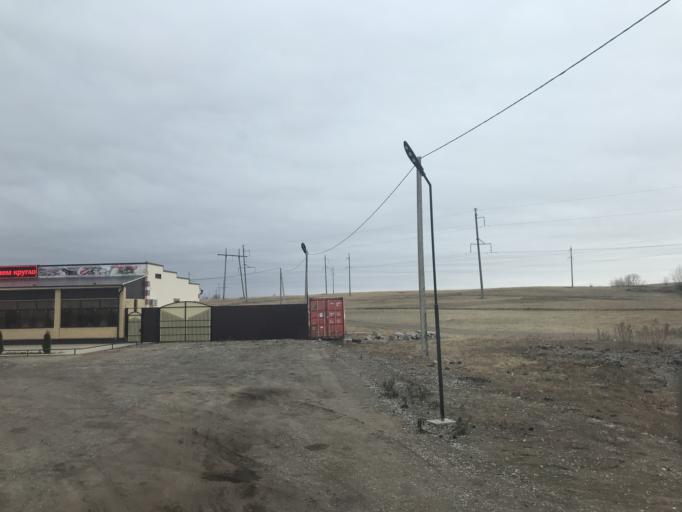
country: KZ
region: Batys Qazaqstan
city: Krugloozernoe
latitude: 51.1623
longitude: 51.2790
